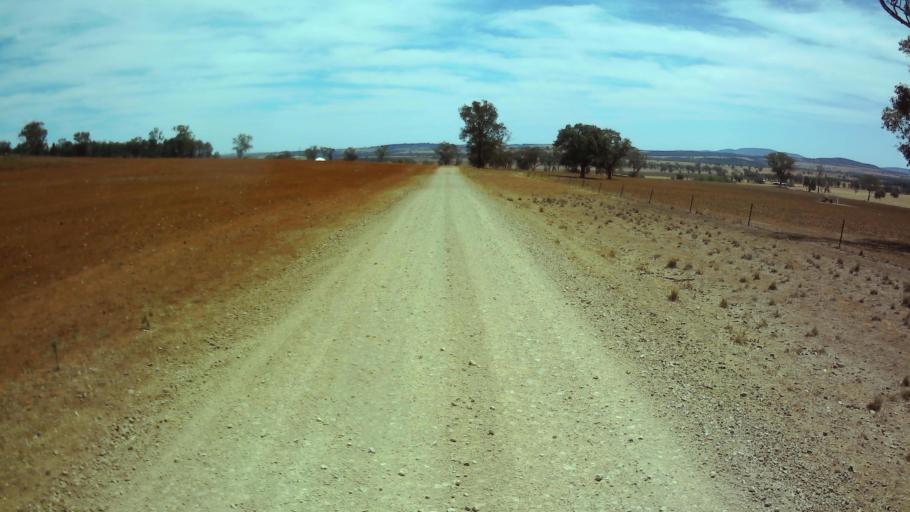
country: AU
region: New South Wales
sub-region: Weddin
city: Grenfell
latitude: -33.7492
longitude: 148.1622
